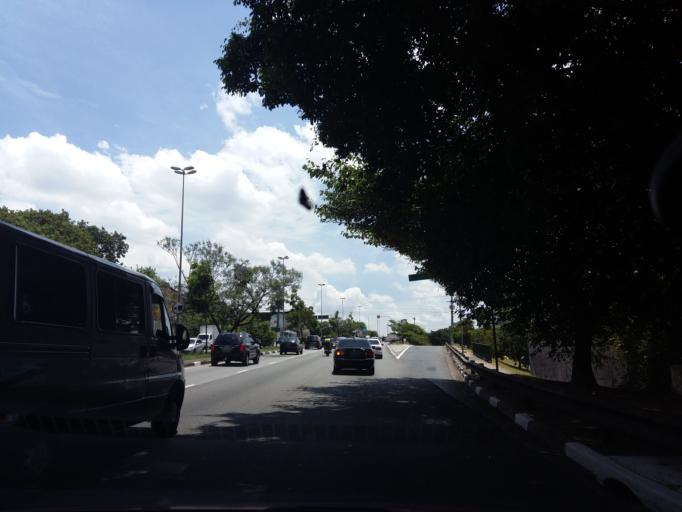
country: BR
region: Sao Paulo
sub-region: Sao Caetano Do Sul
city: Sao Caetano do Sul
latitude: -23.6237
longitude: -46.6133
